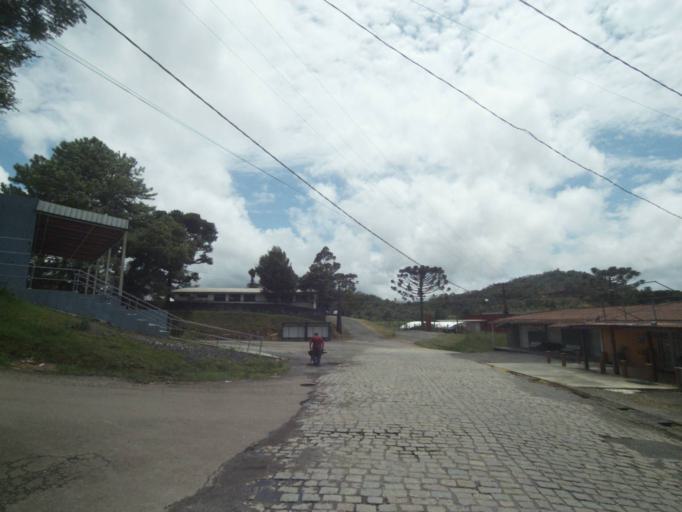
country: BR
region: Parana
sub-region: Campina Grande Do Sul
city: Campina Grande do Sul
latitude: -25.1084
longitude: -48.8079
